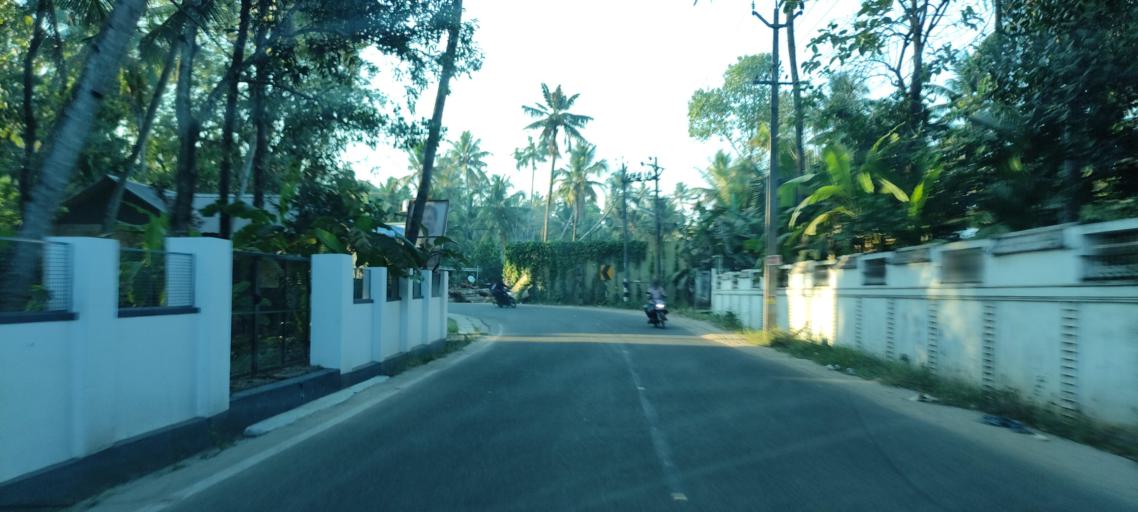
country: IN
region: Kerala
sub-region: Alappuzha
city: Kayankulam
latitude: 9.1769
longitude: 76.4931
